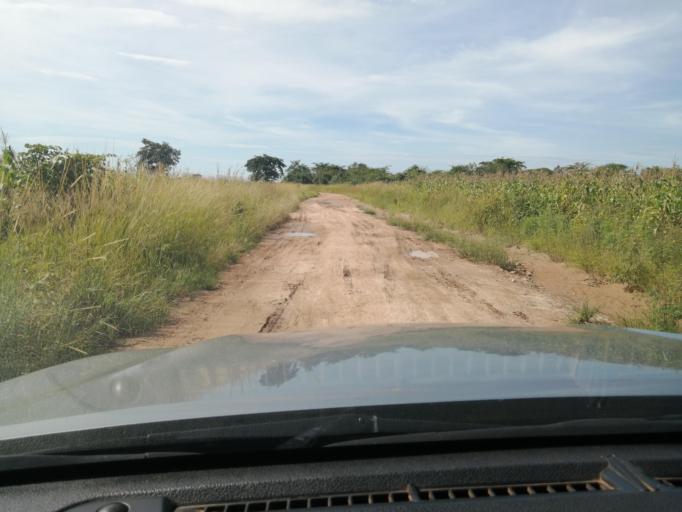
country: ZM
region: Central
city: Chibombo
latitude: -14.9281
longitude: 27.7843
